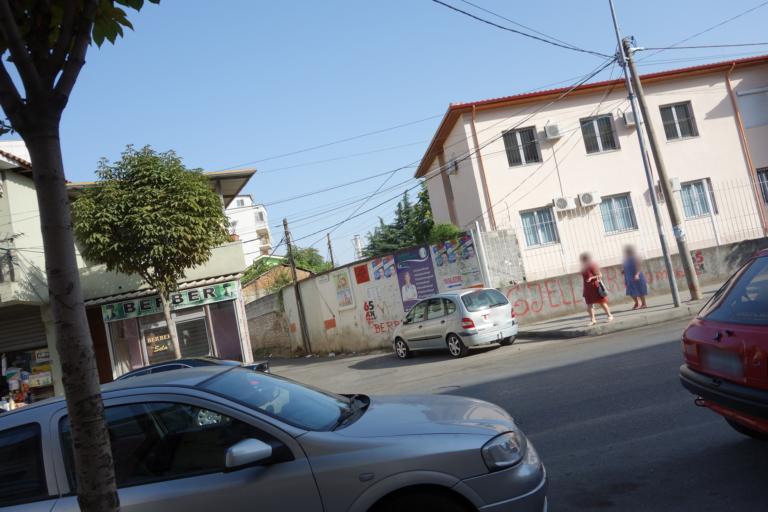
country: AL
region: Tirane
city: Tirana
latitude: 41.3385
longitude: 19.8346
